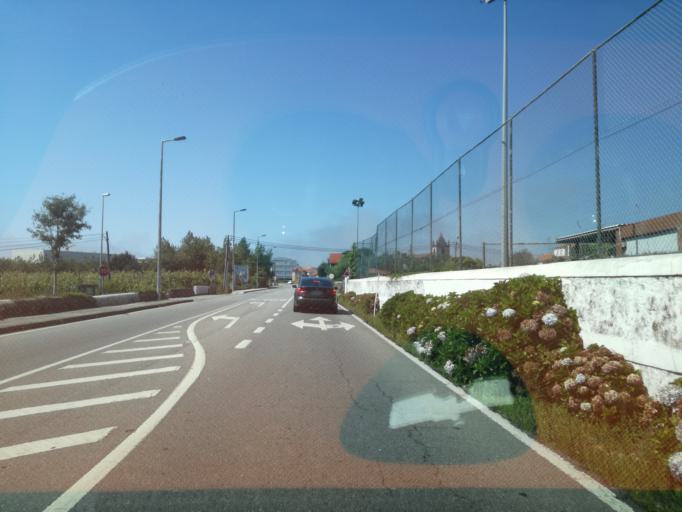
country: PT
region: Braga
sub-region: Esposende
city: Apulia
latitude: 41.5085
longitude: -8.7664
